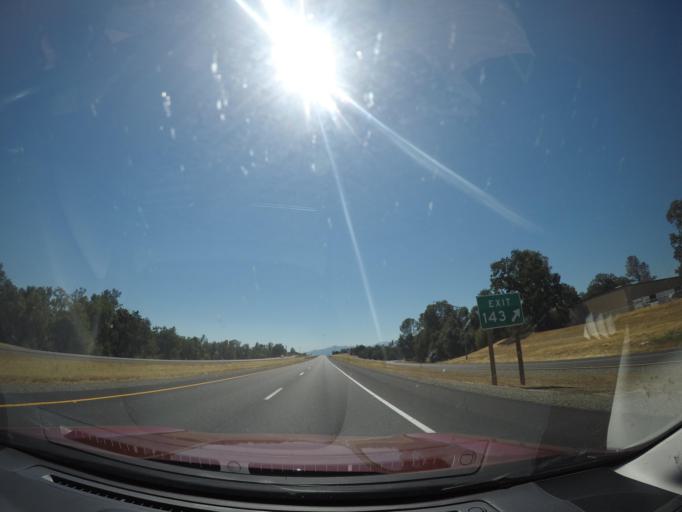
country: US
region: California
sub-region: Shasta County
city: Shasta Lake
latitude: 40.6217
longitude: -122.3154
